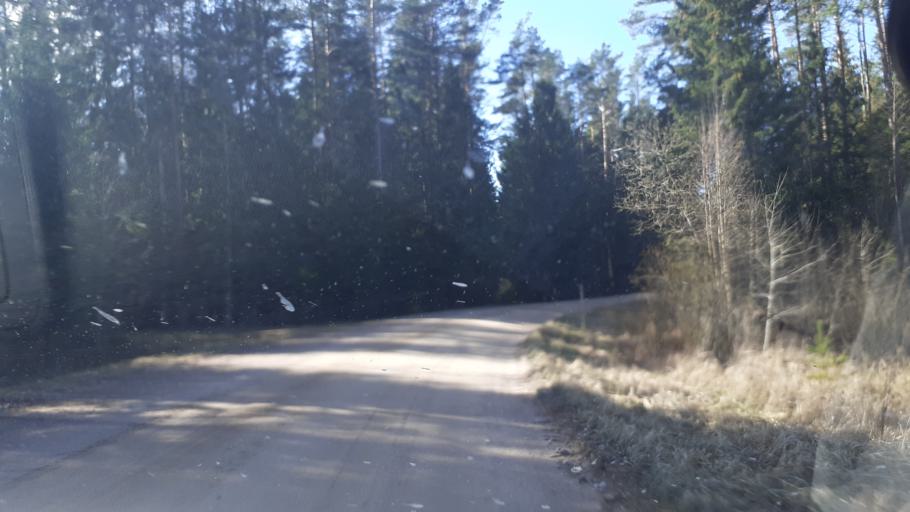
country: LV
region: Kuldigas Rajons
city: Kuldiga
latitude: 56.9124
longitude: 22.0920
